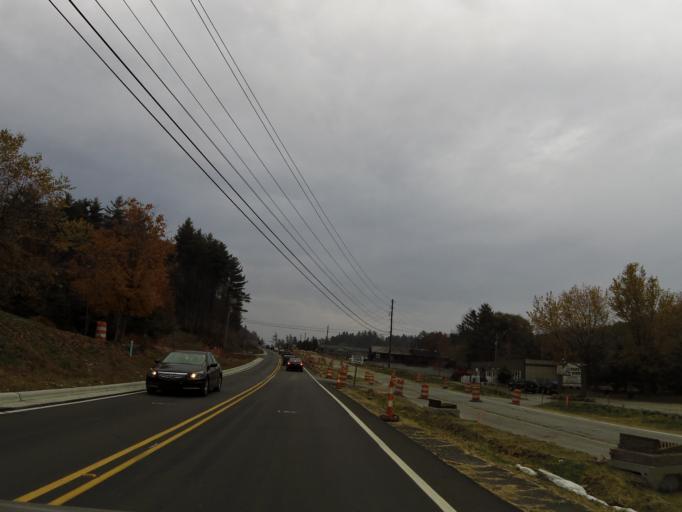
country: US
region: North Carolina
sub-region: Watauga County
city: Blowing Rock
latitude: 36.1297
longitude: -81.6714
